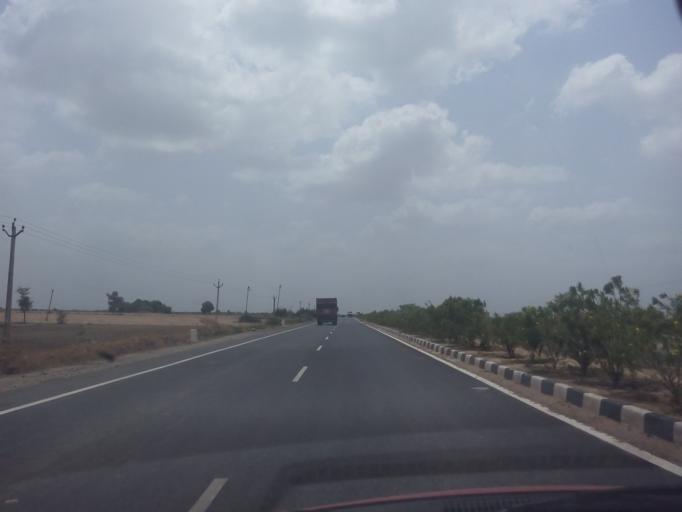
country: IN
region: Gujarat
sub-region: Ahmadabad
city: Mandal
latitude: 23.0844
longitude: 71.8968
